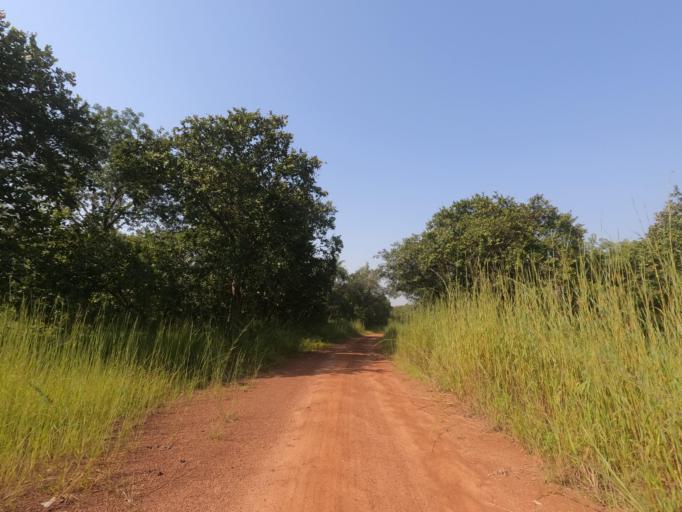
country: SN
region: Sedhiou
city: Sedhiou
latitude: 12.4371
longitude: -15.7382
